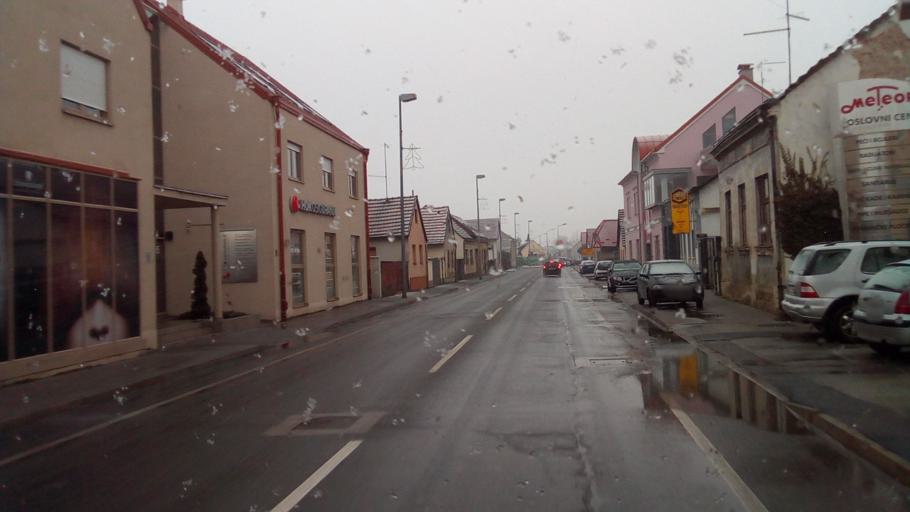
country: HR
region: Varazdinska
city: Varazdin
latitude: 46.3124
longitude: 16.3308
